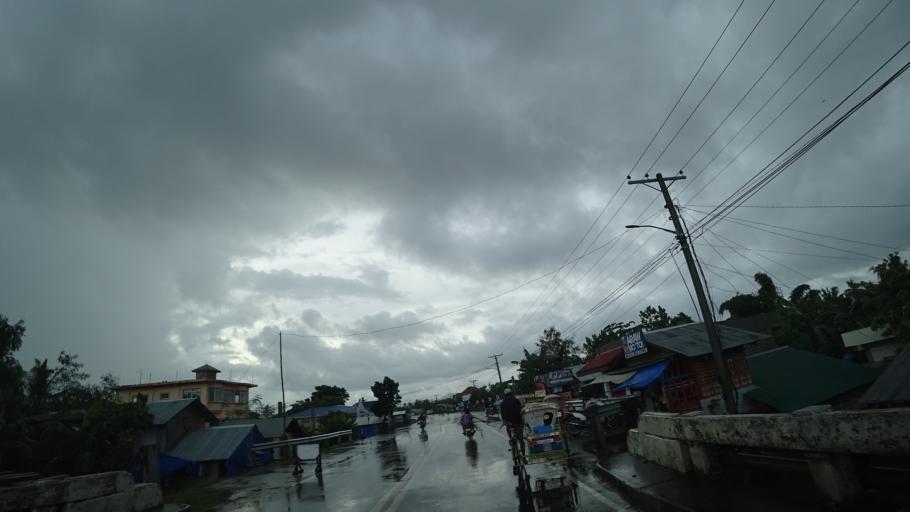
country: PH
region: Eastern Visayas
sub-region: Province of Leyte
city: Tanauan
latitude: 11.1214
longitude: 125.0158
